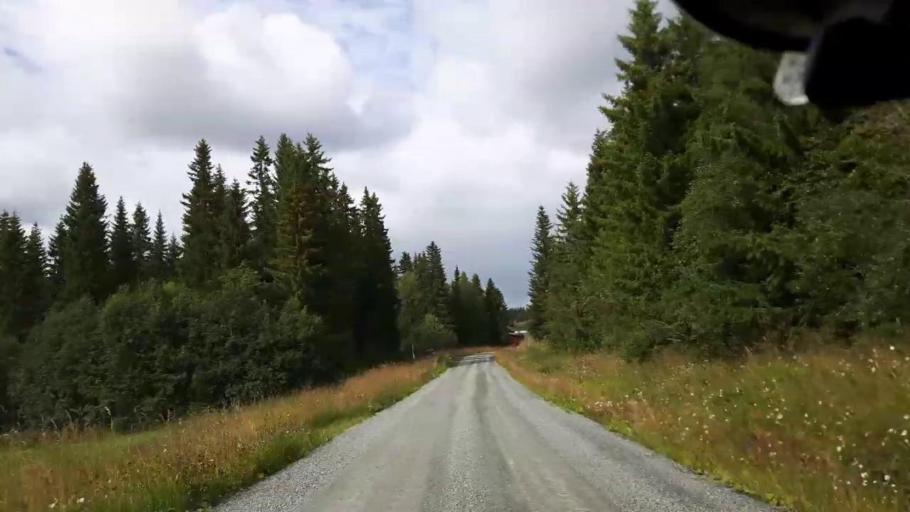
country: SE
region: Jaemtland
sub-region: Krokoms Kommun
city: Valla
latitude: 63.5756
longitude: 13.9056
